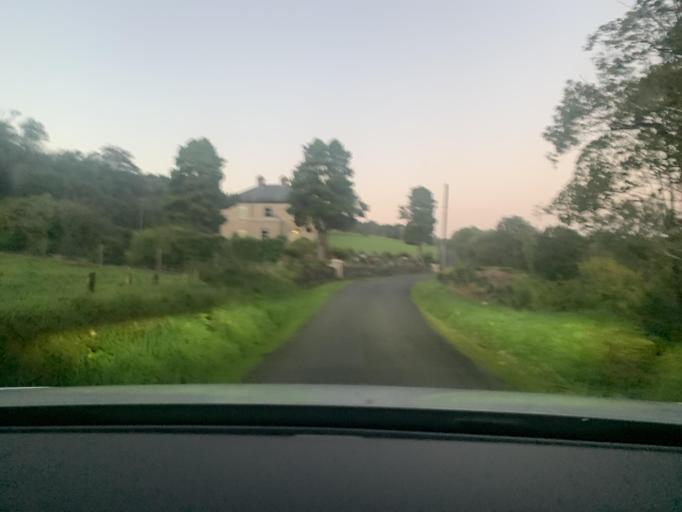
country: IE
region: Connaught
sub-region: County Leitrim
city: Manorhamilton
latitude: 54.2643
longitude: -8.2926
